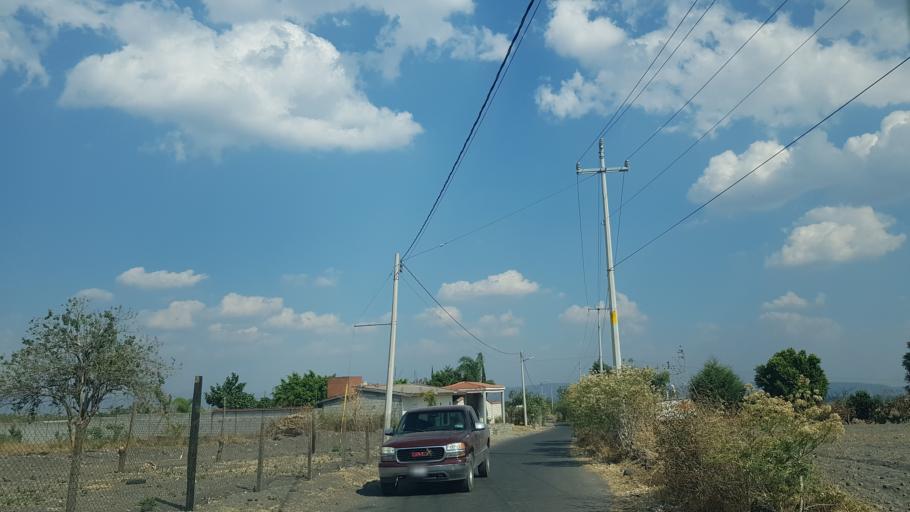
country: MX
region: Puebla
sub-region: Atlixco
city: Colonia Agricola de Ocotepec (Colonia San Jose)
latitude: 18.8936
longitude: -98.5100
